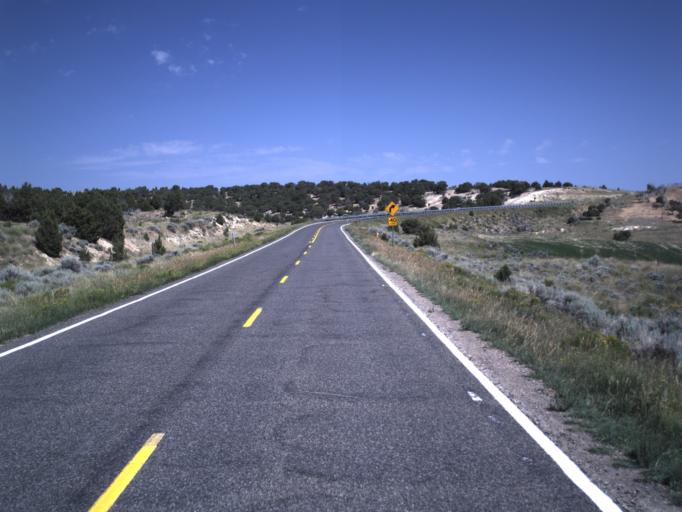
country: US
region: Utah
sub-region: Daggett County
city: Manila
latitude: 40.9883
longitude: -109.8439
